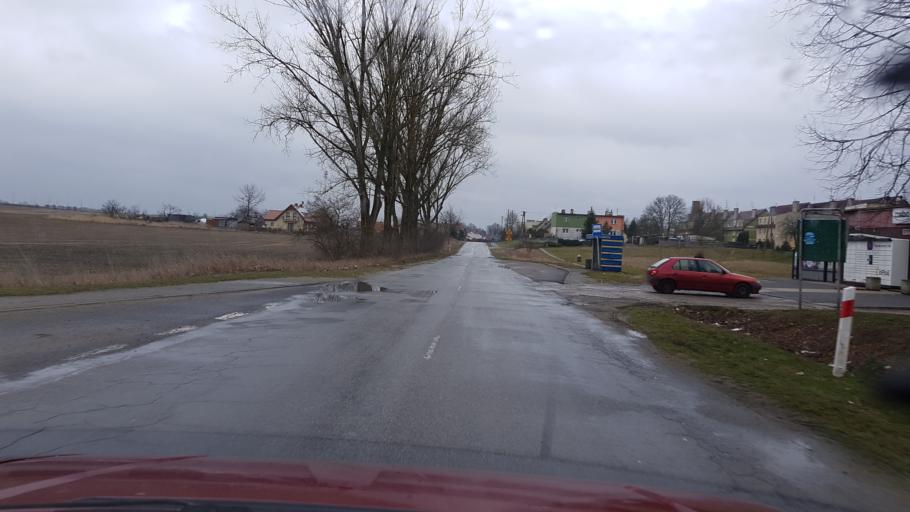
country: PL
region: West Pomeranian Voivodeship
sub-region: Powiat pyrzycki
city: Bielice
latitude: 53.2650
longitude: 14.6166
